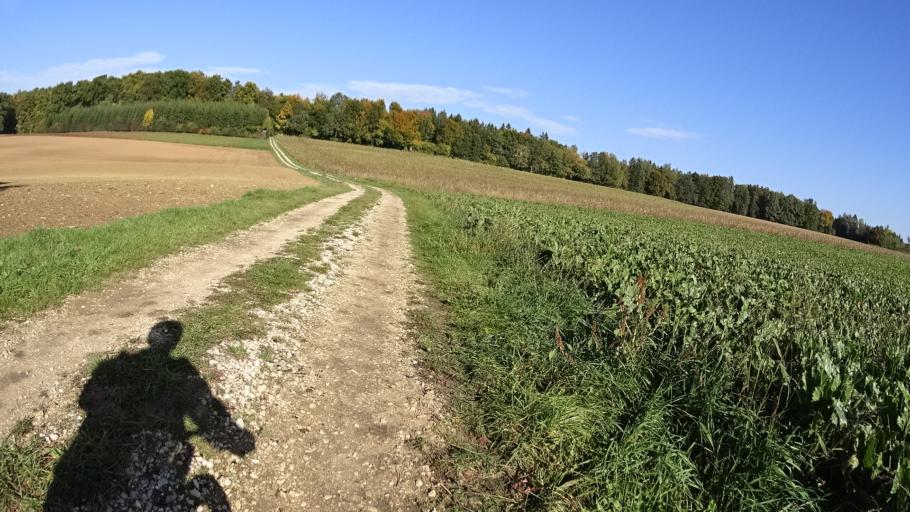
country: DE
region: Bavaria
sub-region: Upper Bavaria
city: Bohmfeld
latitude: 48.8706
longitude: 11.3566
